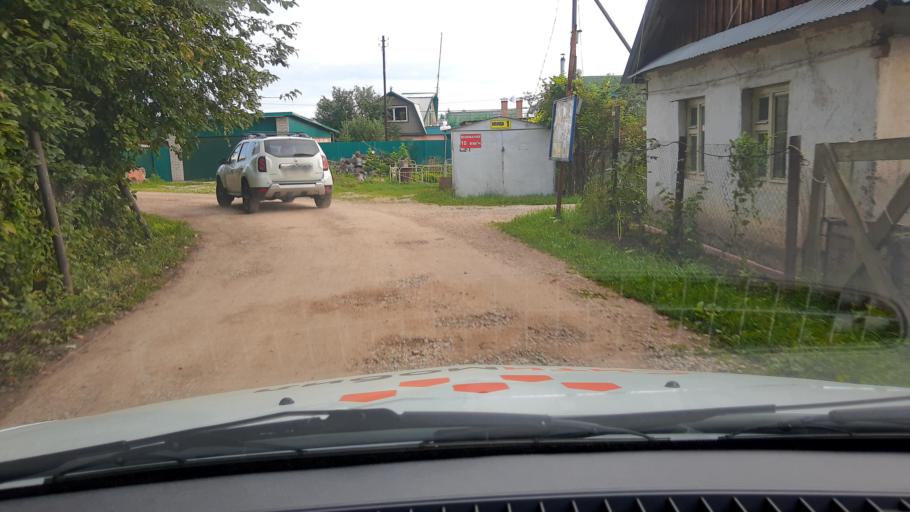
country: RU
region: Bashkortostan
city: Kabakovo
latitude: 54.7104
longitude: 56.1391
